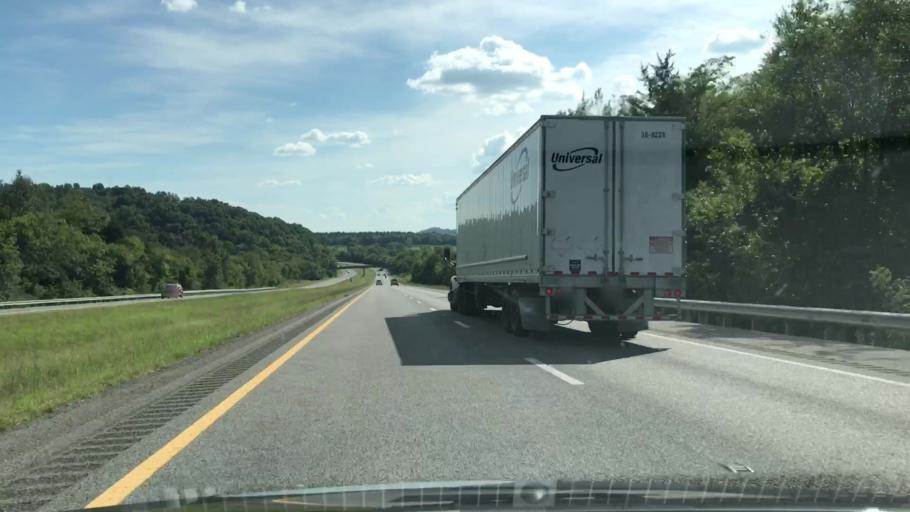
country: US
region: Alabama
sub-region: Limestone County
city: Ardmore
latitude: 35.1134
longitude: -86.8818
